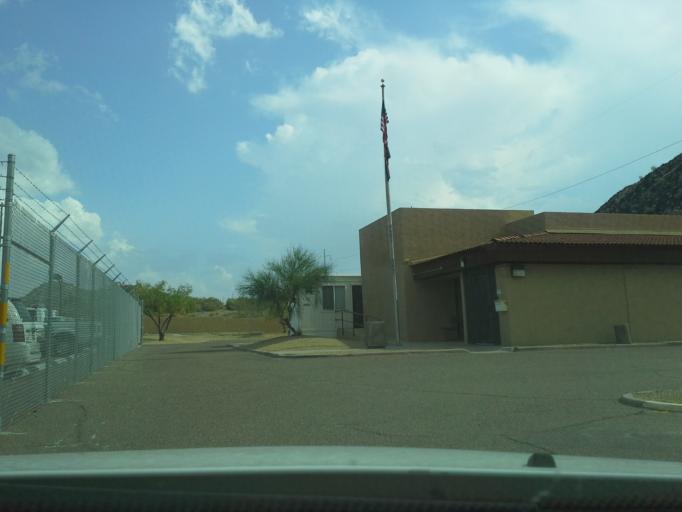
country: US
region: Arizona
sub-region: Maricopa County
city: Glendale
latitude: 33.6051
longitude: -112.0644
